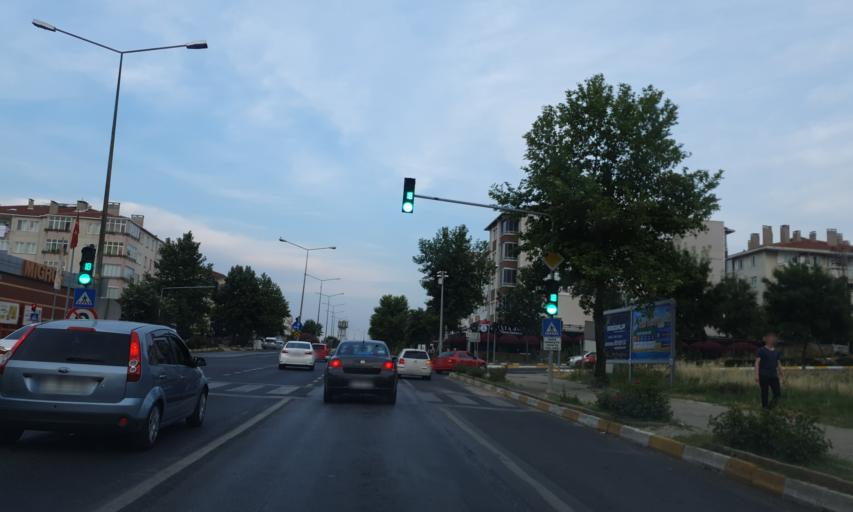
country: TR
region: Kirklareli
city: Luleburgaz
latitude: 41.4012
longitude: 27.3706
